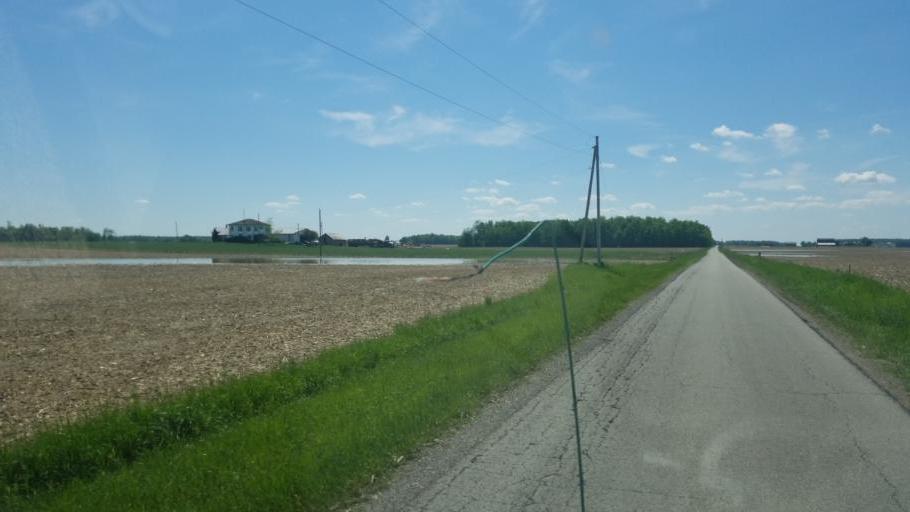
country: US
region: Ohio
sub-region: Crawford County
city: Bucyrus
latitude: 40.9795
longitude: -82.9987
